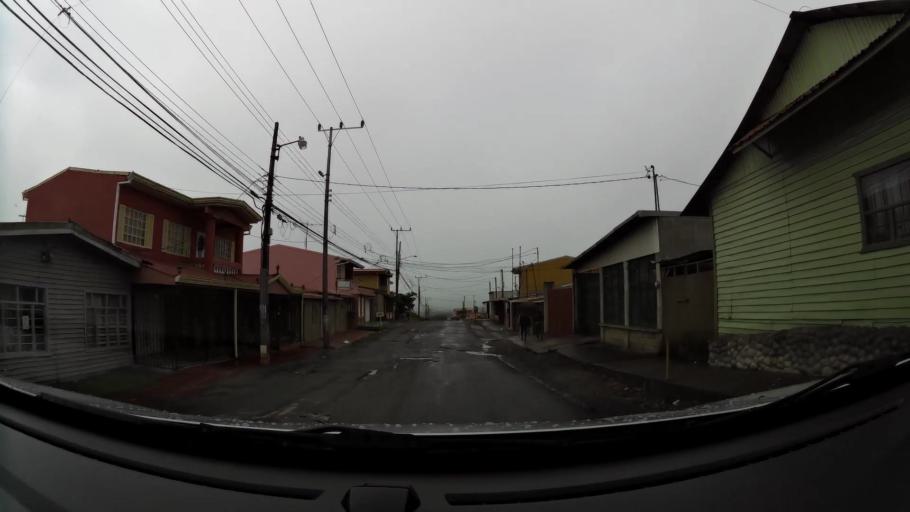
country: CR
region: Cartago
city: Paraiso
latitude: 9.8374
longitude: -83.8649
